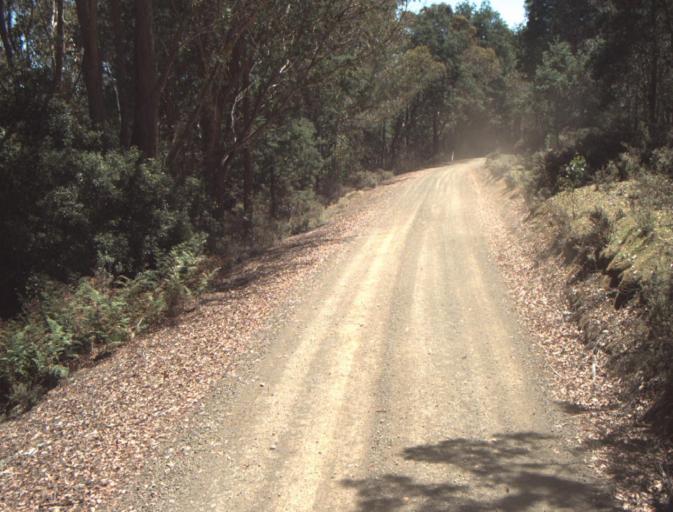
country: AU
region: Tasmania
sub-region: Dorset
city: Scottsdale
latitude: -41.3560
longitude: 147.4255
